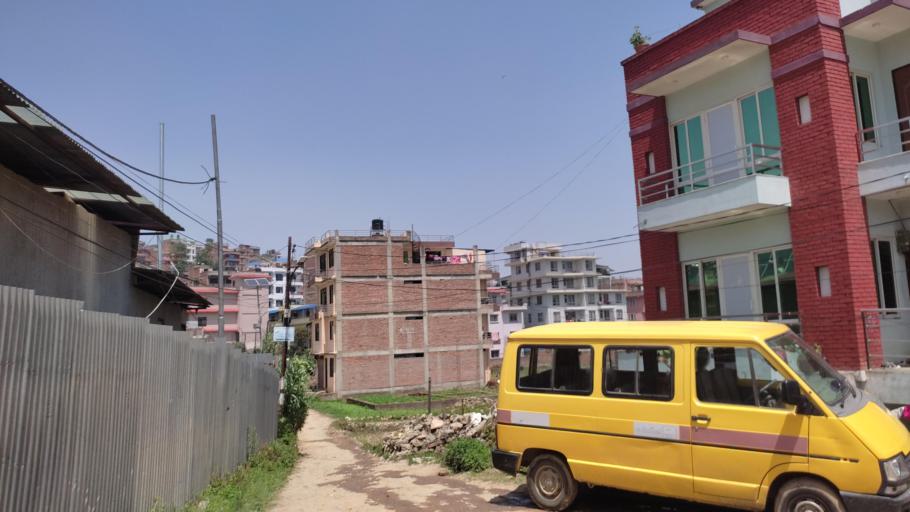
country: NP
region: Central Region
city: Kirtipur
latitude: 27.6750
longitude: 85.2752
